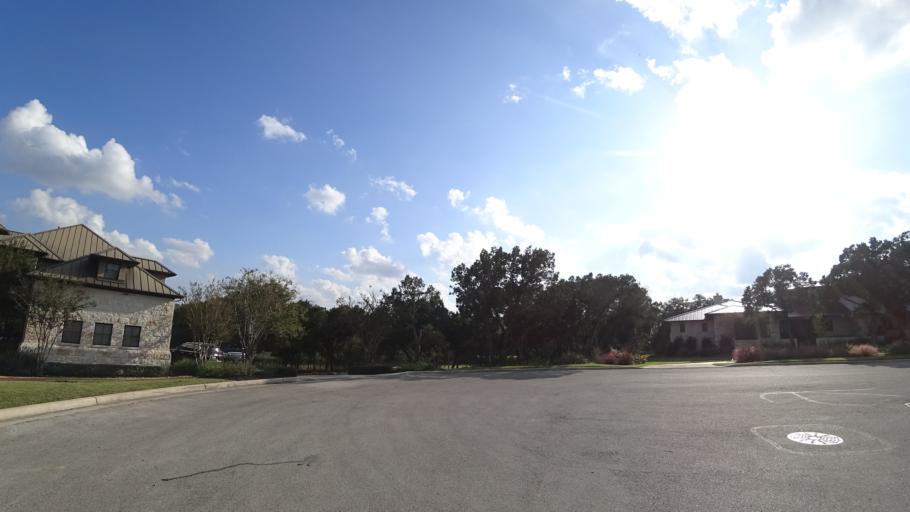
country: US
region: Texas
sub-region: Travis County
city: Barton Creek
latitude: 30.2768
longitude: -97.8795
